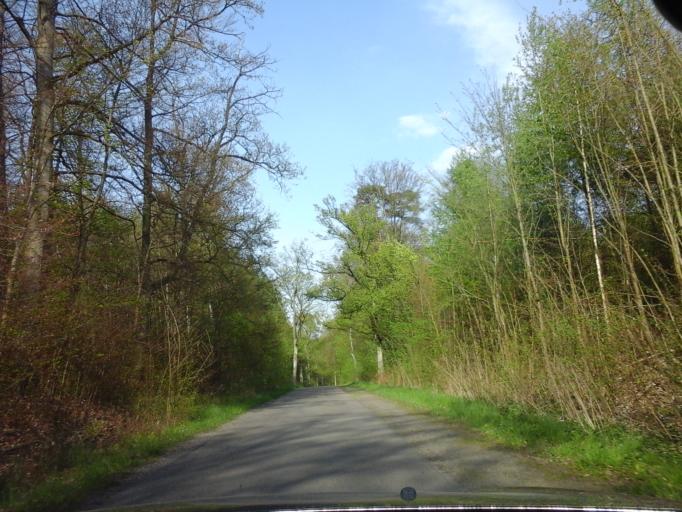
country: PL
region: West Pomeranian Voivodeship
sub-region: Powiat choszczenski
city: Krzecin
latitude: 53.0457
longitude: 15.5671
